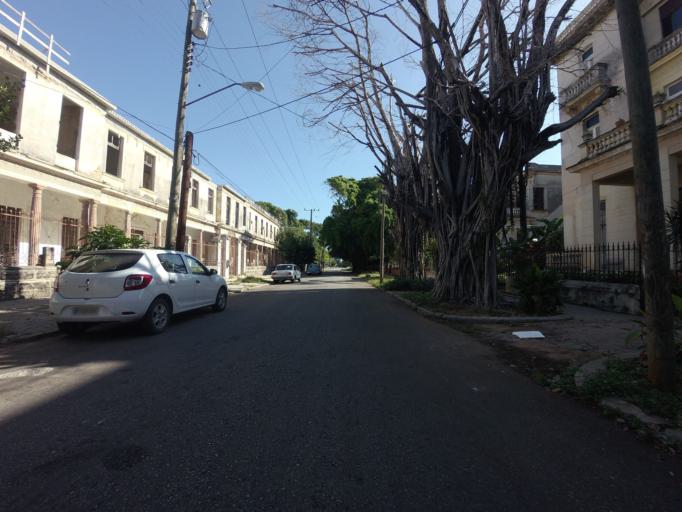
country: CU
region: La Habana
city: Havana
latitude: 23.1372
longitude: -82.3960
